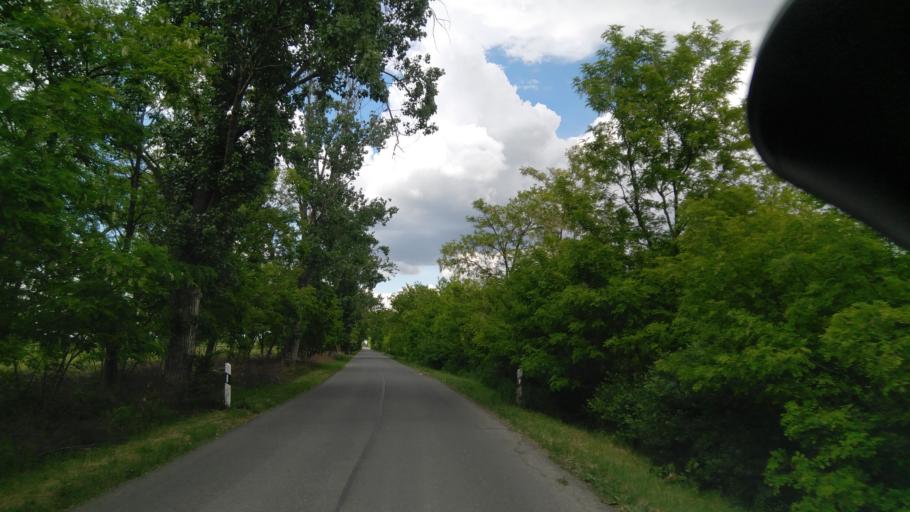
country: HU
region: Bekes
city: Bucsa
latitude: 47.1579
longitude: 21.0822
